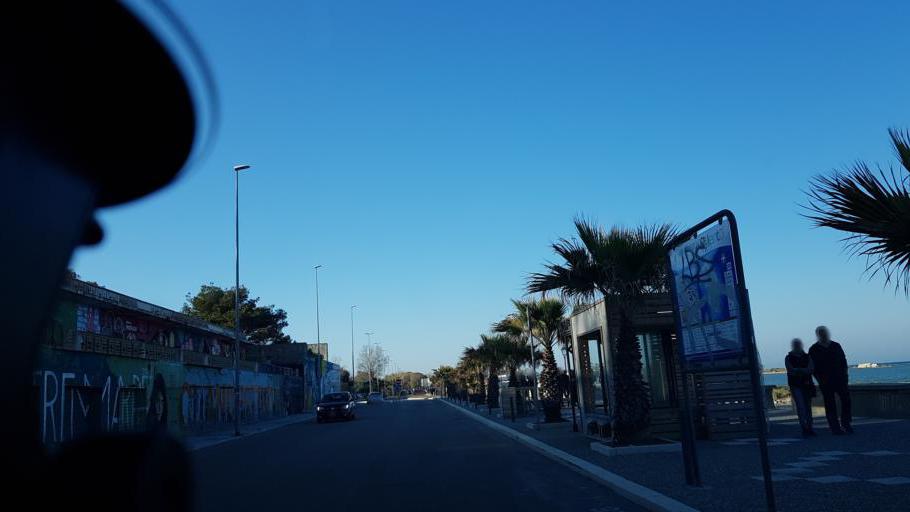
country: IT
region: Apulia
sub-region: Provincia di Lecce
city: Struda
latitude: 40.3846
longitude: 18.3048
